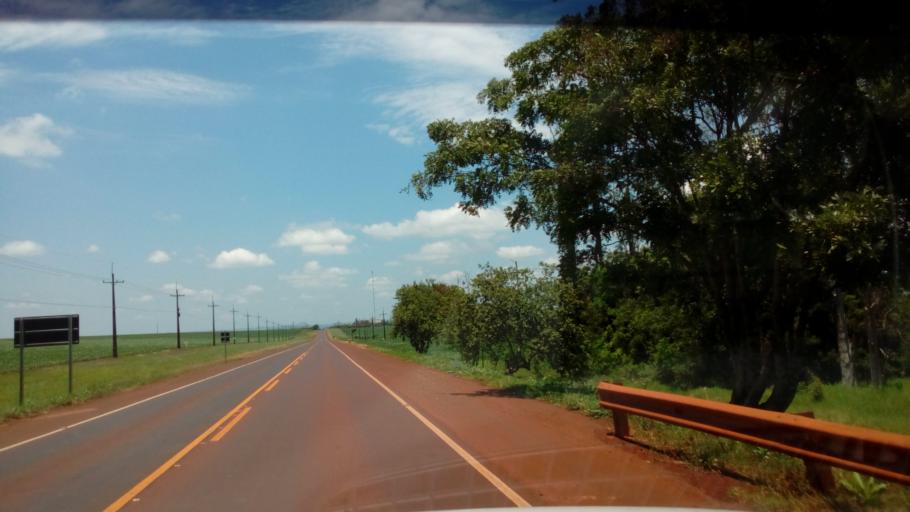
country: PY
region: Alto Parana
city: Naranjal
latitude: -25.9989
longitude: -55.1233
